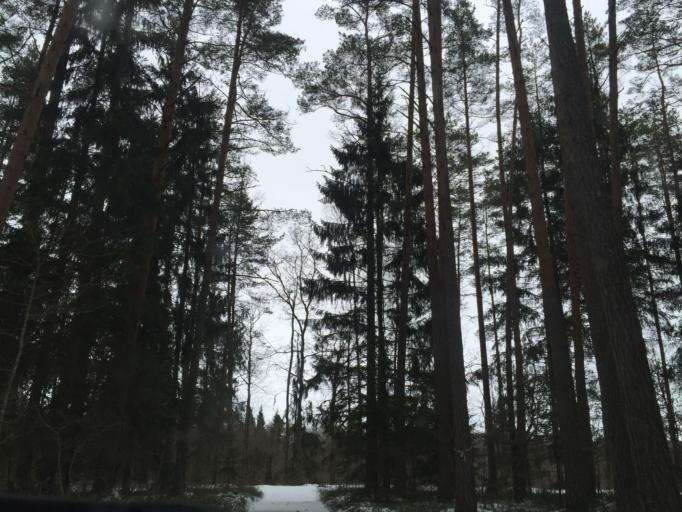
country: LV
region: Krimulda
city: Ragana
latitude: 57.1404
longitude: 24.7293
